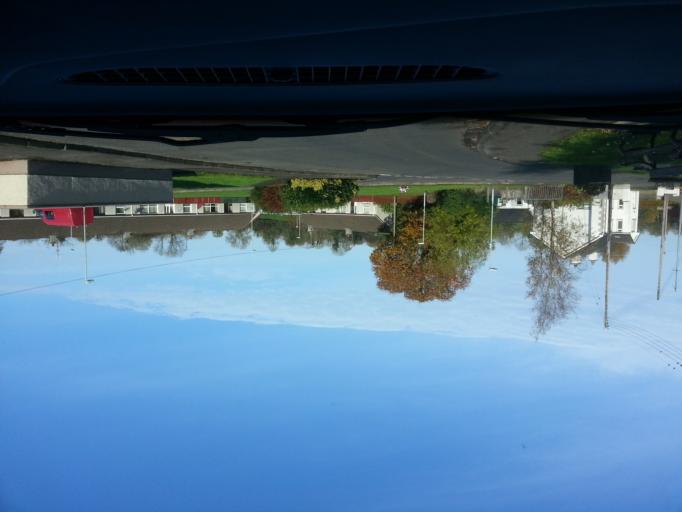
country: GB
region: Northern Ireland
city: Lisnaskea
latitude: 54.2184
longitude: -7.3923
